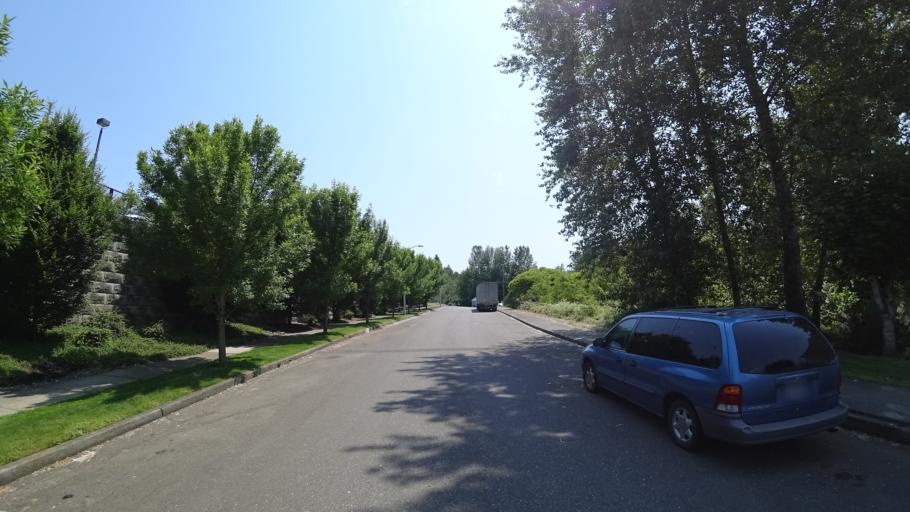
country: US
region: Oregon
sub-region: Multnomah County
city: Lents
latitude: 45.4549
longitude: -122.5697
